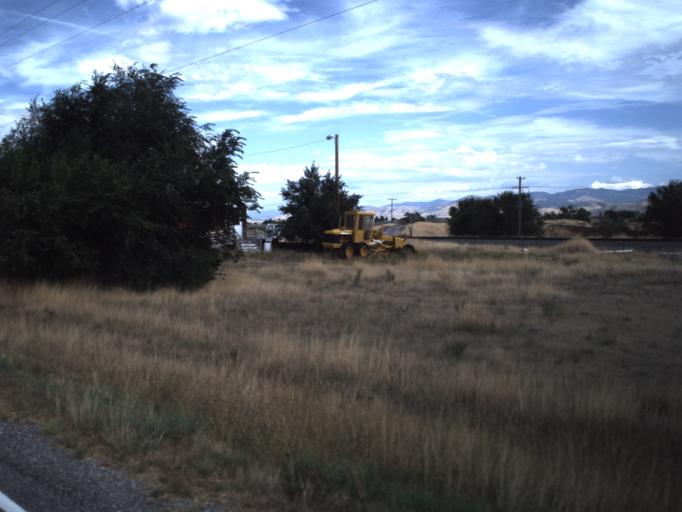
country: US
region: Utah
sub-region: Cache County
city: Lewiston
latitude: 41.9910
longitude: -111.9547
